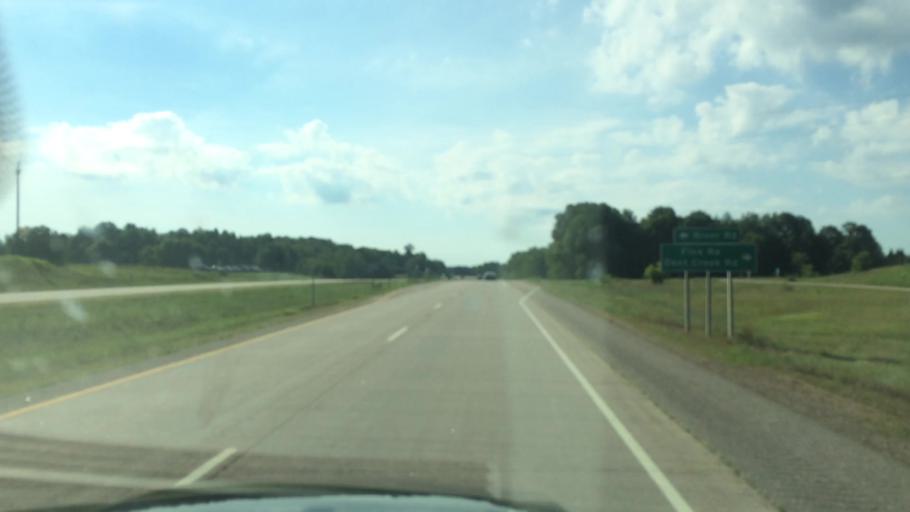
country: US
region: Wisconsin
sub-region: Shawano County
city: Wittenberg
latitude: 44.8114
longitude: -89.0428
